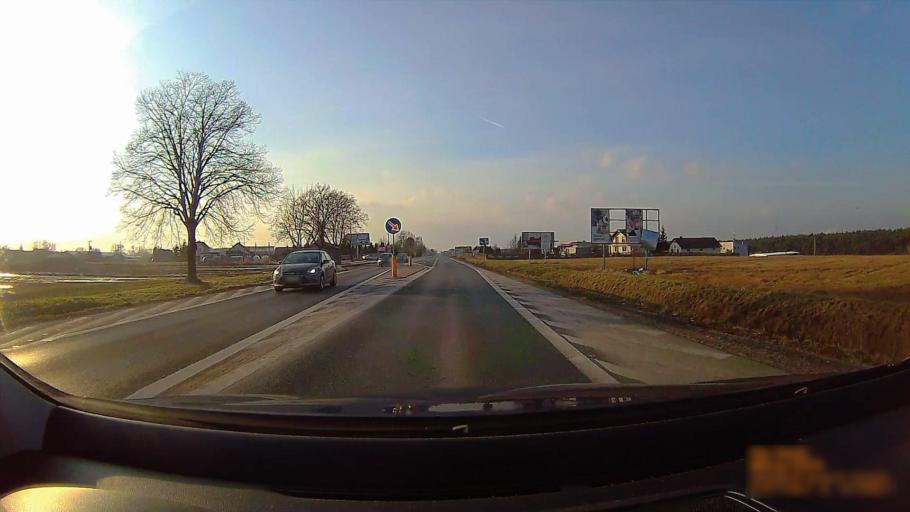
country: PL
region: Greater Poland Voivodeship
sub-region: Konin
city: Konin
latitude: 52.1940
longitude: 18.3164
